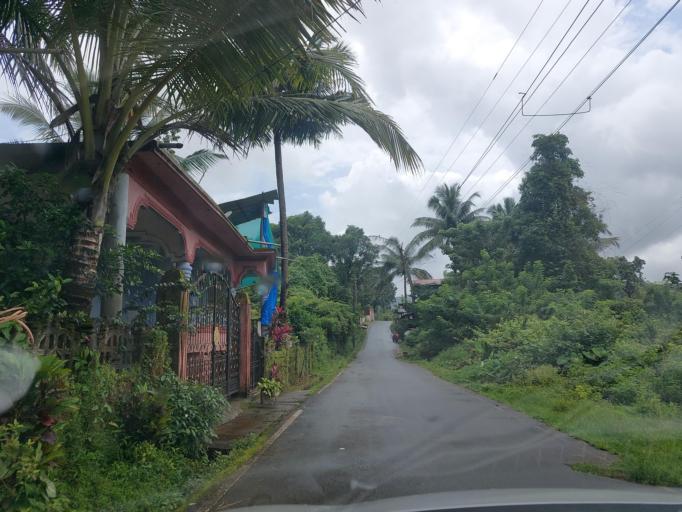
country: IN
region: Goa
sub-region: North Goa
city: Valpoy
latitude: 15.5384
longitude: 74.1417
